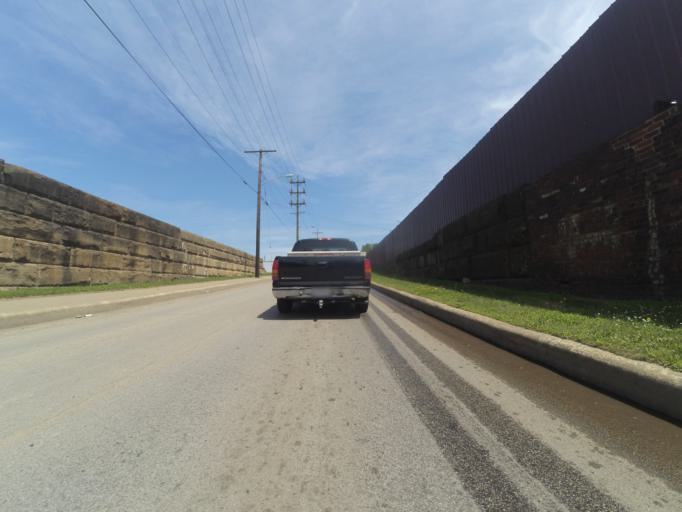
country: US
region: Ohio
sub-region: Cuyahoga County
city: Newburgh Heights
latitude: 41.4592
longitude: -81.6280
